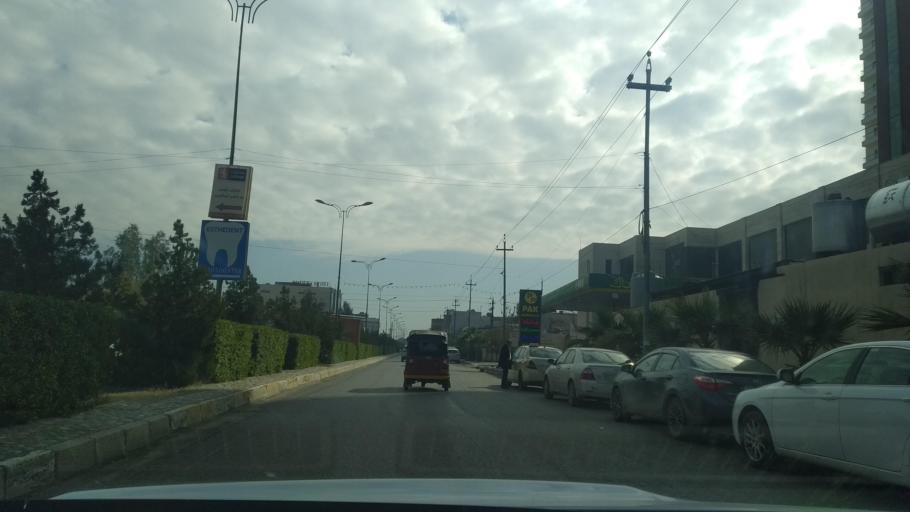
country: IQ
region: Arbil
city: Erbil
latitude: 36.1800
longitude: 44.0259
